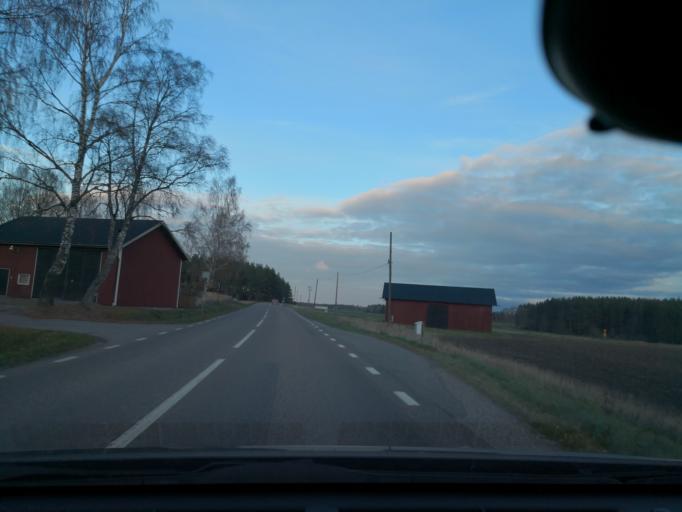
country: SE
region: Vaestmanland
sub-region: Vasteras
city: Tillberga
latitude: 59.6332
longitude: 16.6629
